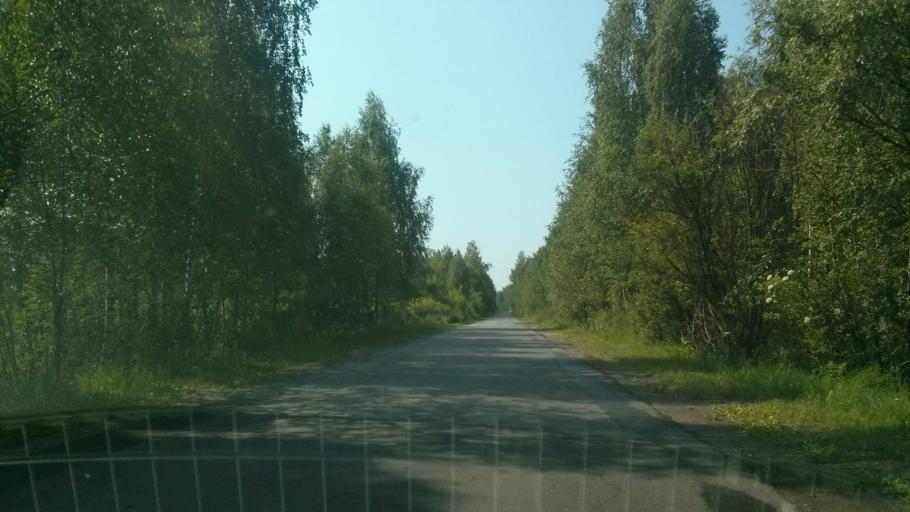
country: RU
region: Vladimir
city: Murom
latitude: 55.5248
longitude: 42.0226
